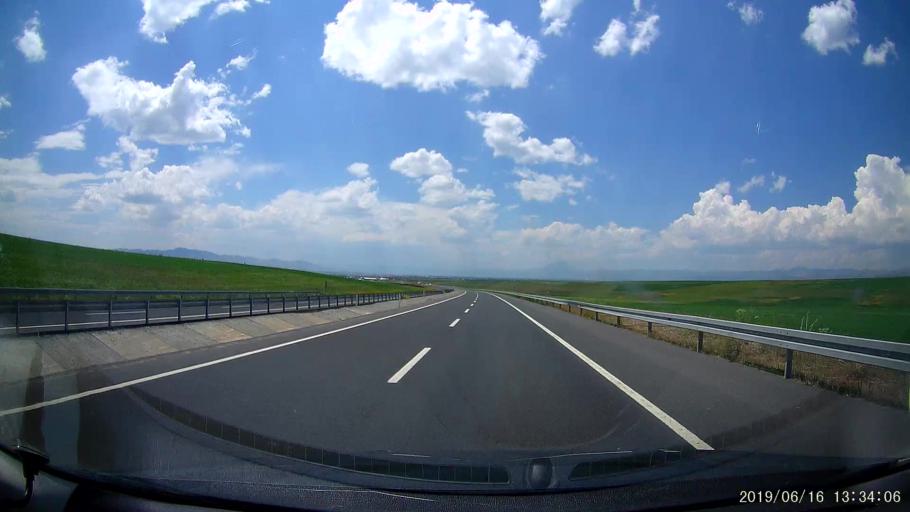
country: TR
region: Agri
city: Agri
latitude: 39.7112
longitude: 43.1363
